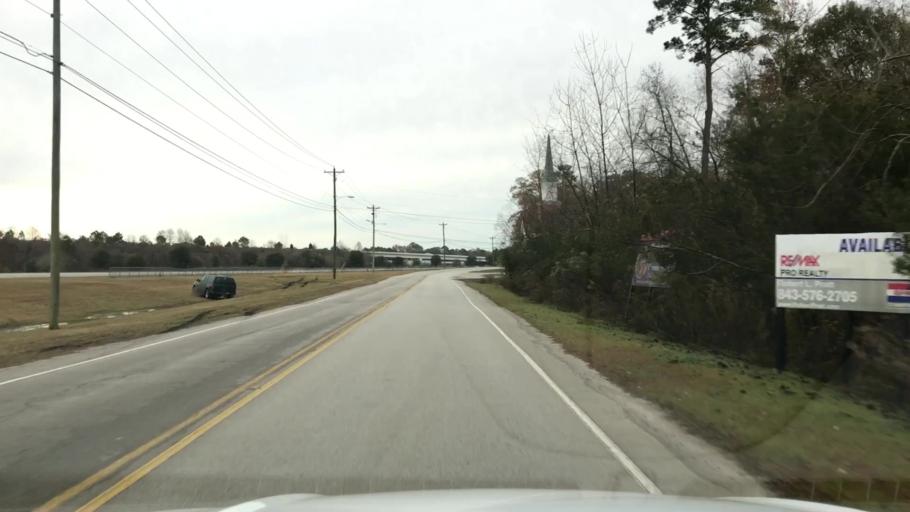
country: US
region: South Carolina
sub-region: Berkeley County
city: Goose Creek
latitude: 32.9724
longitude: -80.0519
